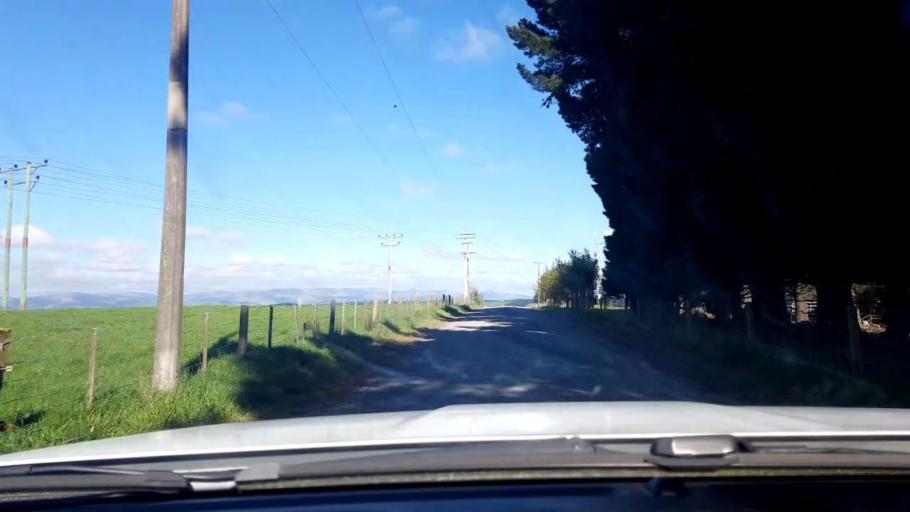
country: NZ
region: Otago
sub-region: Clutha District
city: Balclutha
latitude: -46.2238
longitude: 169.7551
